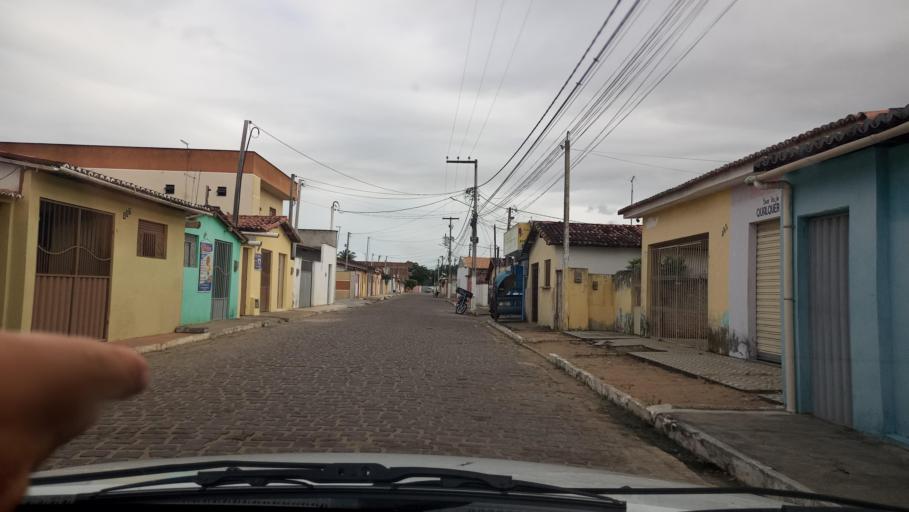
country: BR
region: Rio Grande do Norte
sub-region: Brejinho
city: Brejinho
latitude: -6.0483
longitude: -35.4328
